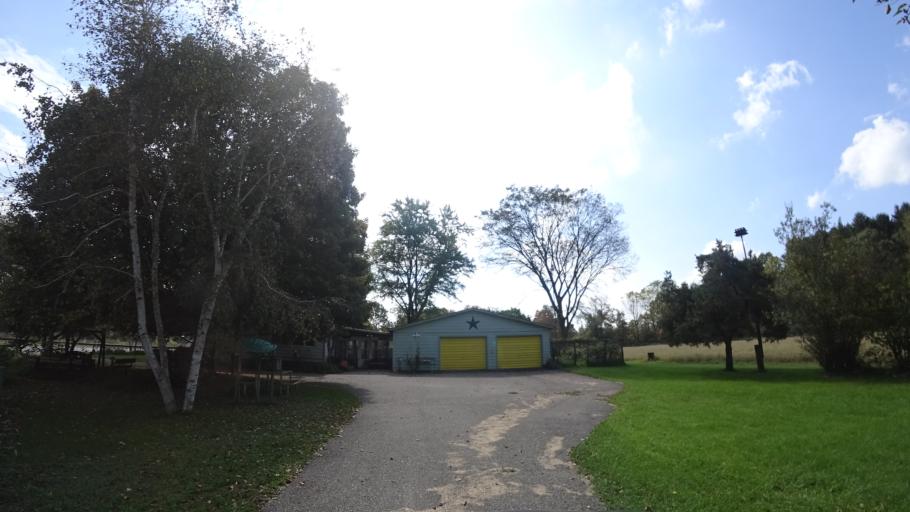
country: US
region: Michigan
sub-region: Saint Joseph County
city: Three Rivers
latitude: 41.9171
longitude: -85.6250
